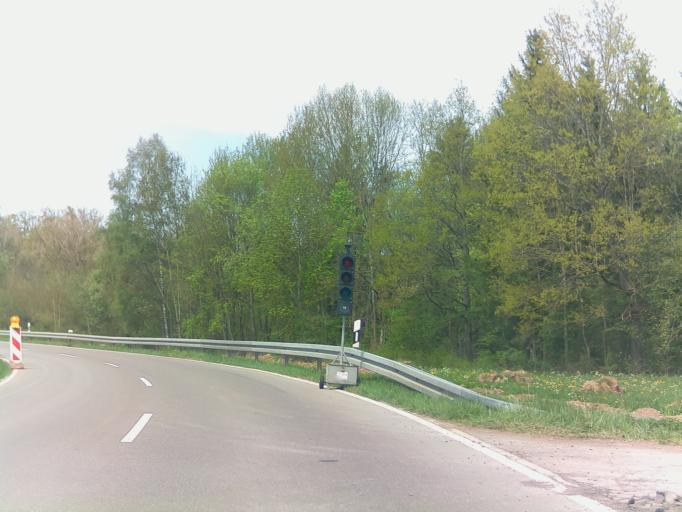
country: DE
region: Baden-Wuerttemberg
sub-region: Freiburg Region
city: Deisslingen
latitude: 48.1354
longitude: 8.6298
